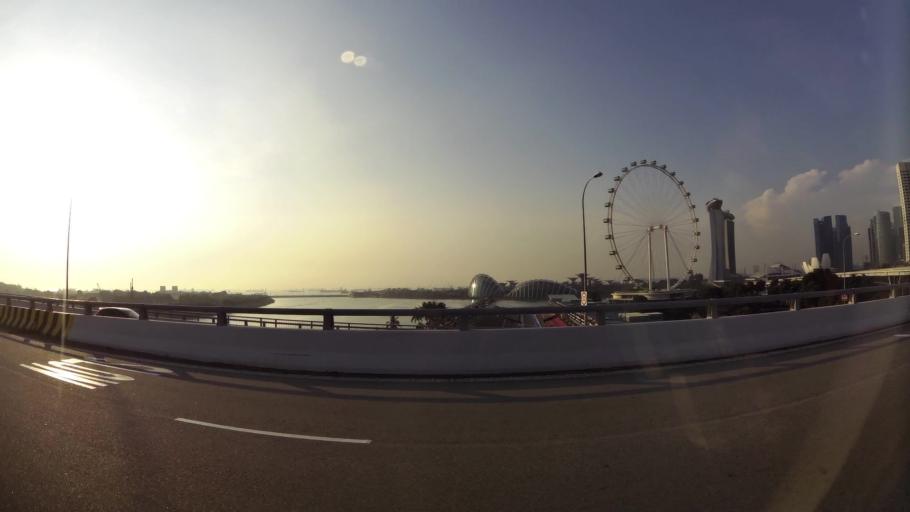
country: SG
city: Singapore
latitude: 1.2937
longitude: 103.8639
